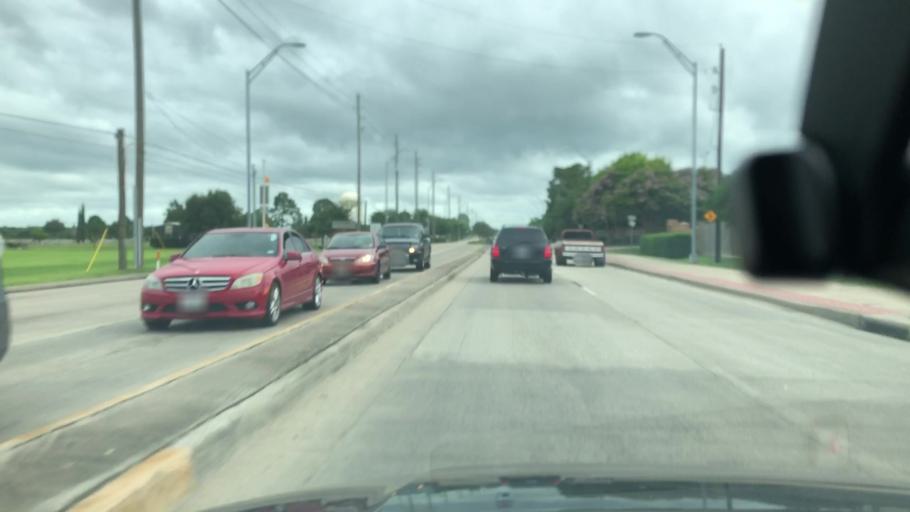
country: US
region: Texas
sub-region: Brazoria County
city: Brookside Village
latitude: 29.5705
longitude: -95.3507
